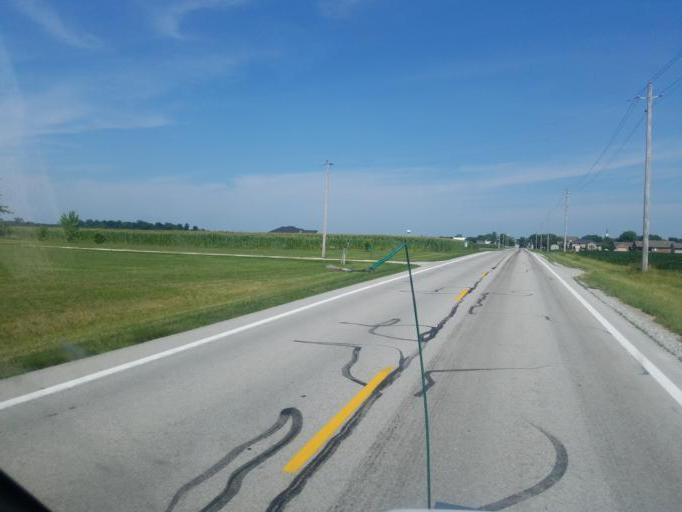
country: US
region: Ohio
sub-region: Auglaize County
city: Saint Marys
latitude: 40.4958
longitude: -84.3298
